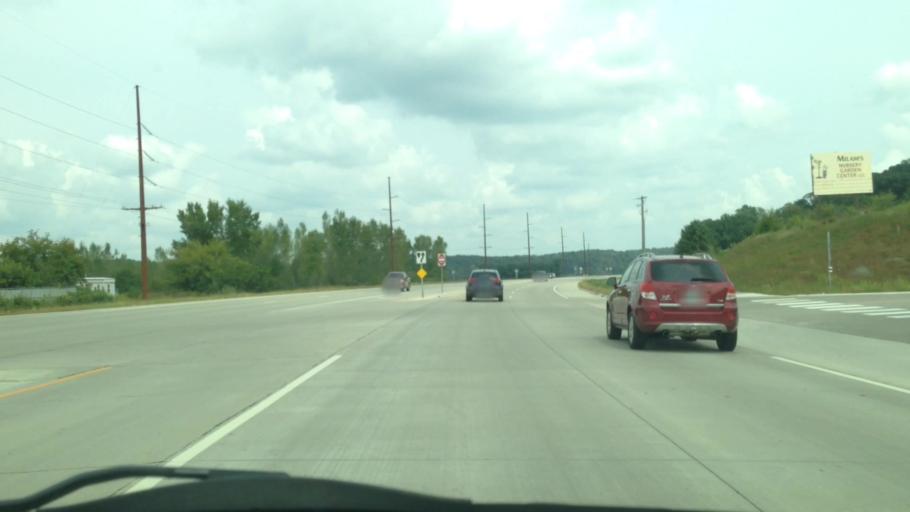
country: US
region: Minnesota
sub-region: Olmsted County
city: Rochester
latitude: 44.0623
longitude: -92.4528
